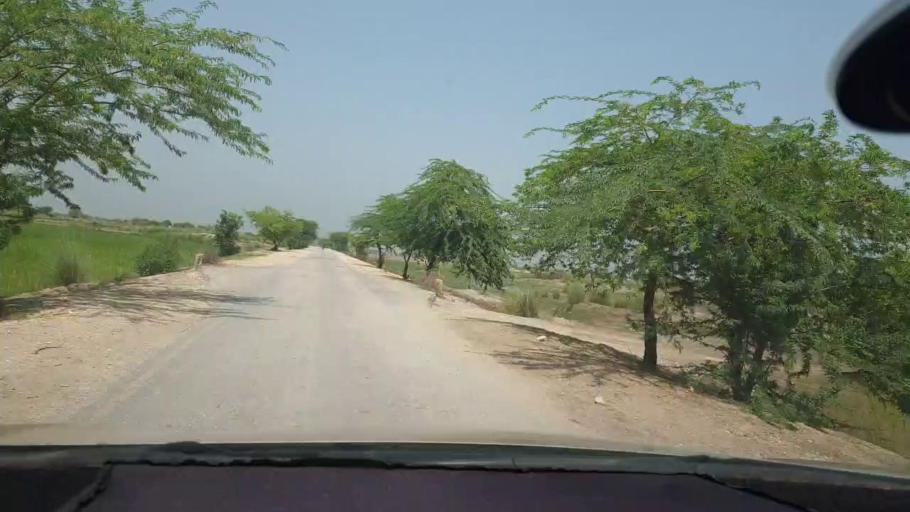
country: PK
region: Sindh
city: Kambar
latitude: 27.6710
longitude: 67.9126
